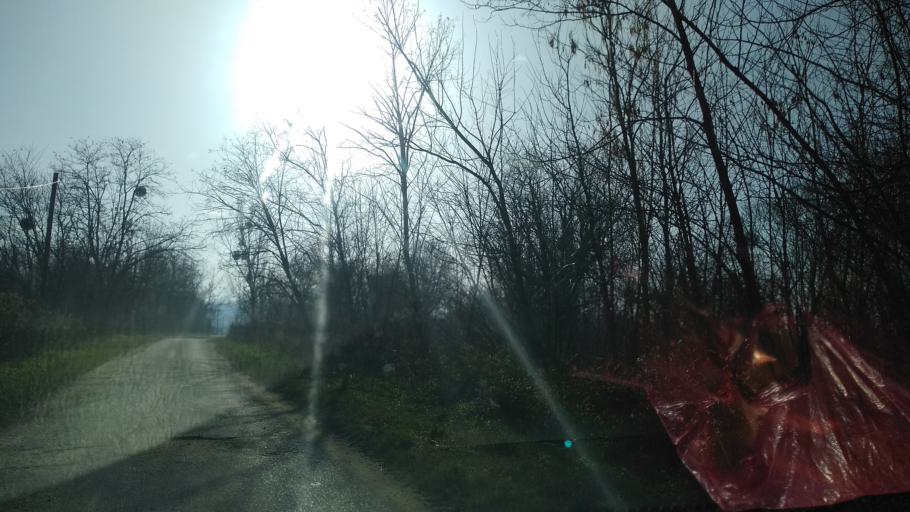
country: HU
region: Somogy
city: Barcs
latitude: 45.9554
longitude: 17.4869
